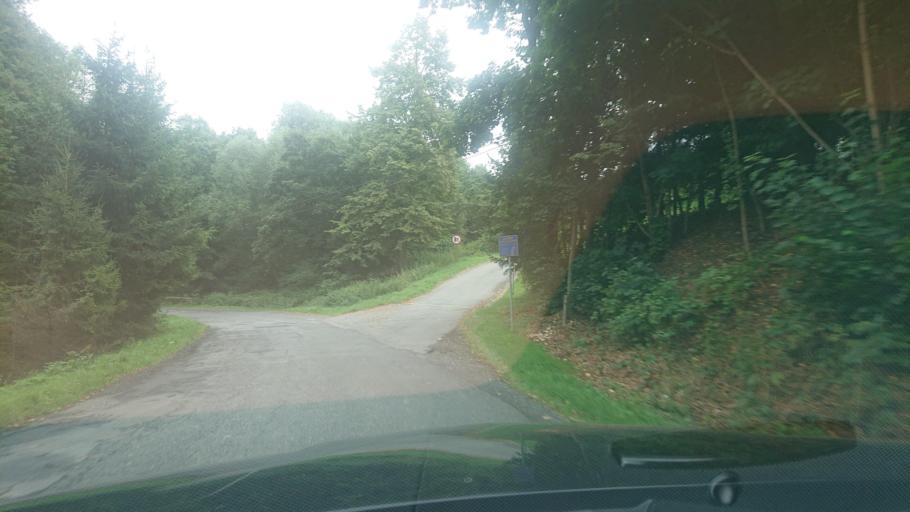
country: PL
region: Lower Silesian Voivodeship
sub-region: Powiat klodzki
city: Bystrzyca Klodzka
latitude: 50.3112
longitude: 16.6988
